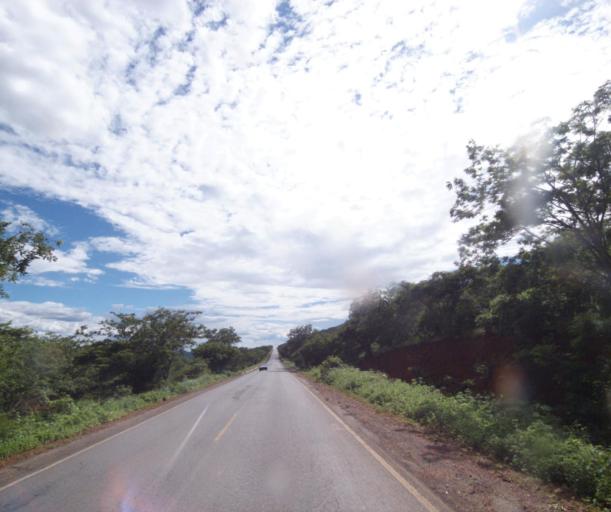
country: BR
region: Minas Gerais
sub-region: Espinosa
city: Espinosa
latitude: -14.7863
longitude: -42.6872
